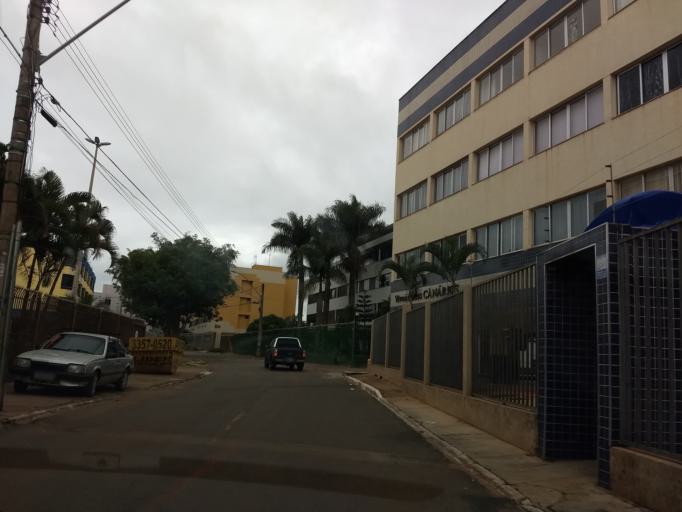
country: BR
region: Federal District
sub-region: Brasilia
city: Brasilia
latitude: -15.8081
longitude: -47.9910
